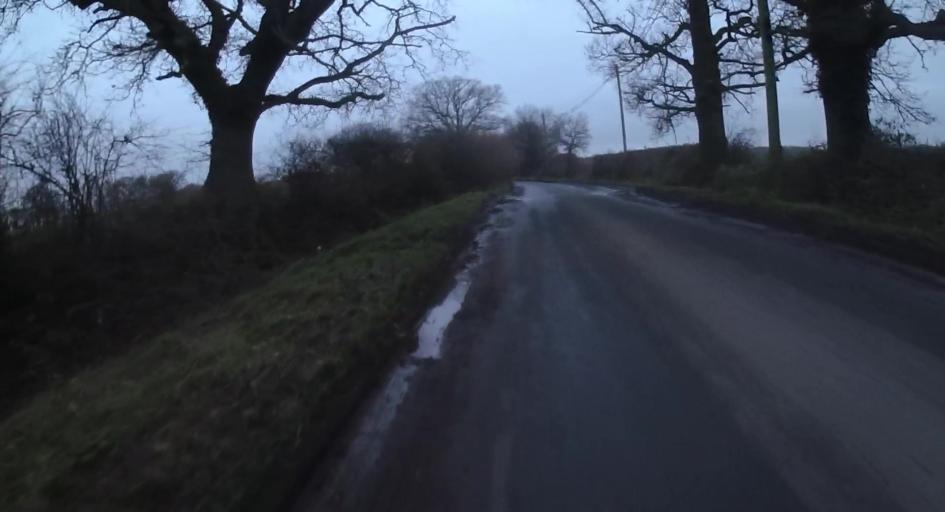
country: GB
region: England
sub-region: Hampshire
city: Tadley
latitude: 51.3324
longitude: -1.0898
